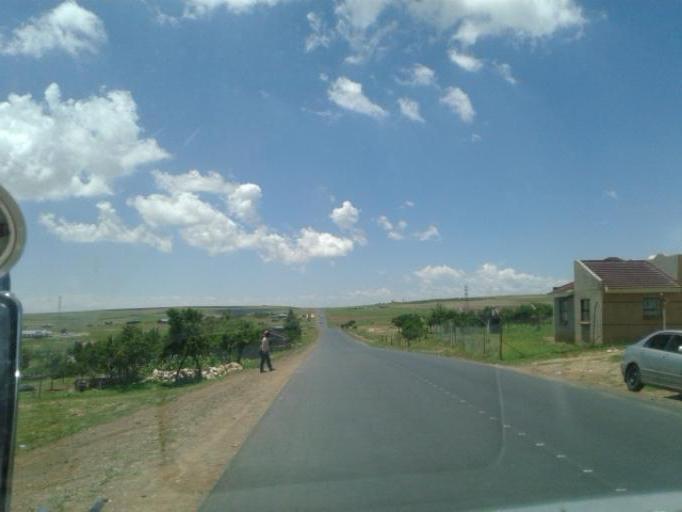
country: LS
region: Maseru
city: Maseru
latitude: -29.3156
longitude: 27.5906
